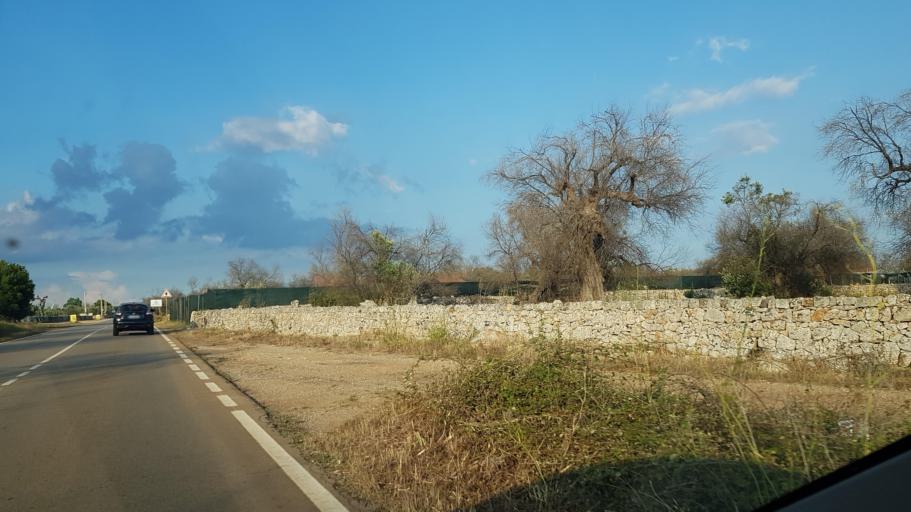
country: IT
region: Apulia
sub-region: Provincia di Lecce
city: Presicce
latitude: 39.8911
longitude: 18.2470
